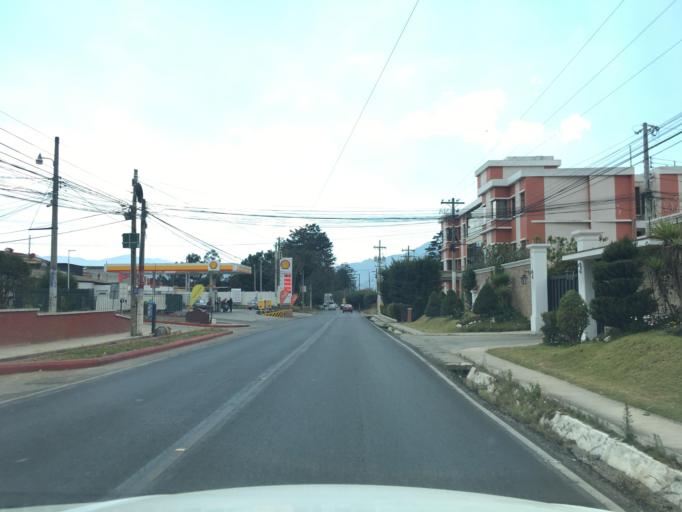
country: GT
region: Quetzaltenango
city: Olintepeque
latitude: 14.8726
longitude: -91.5134
